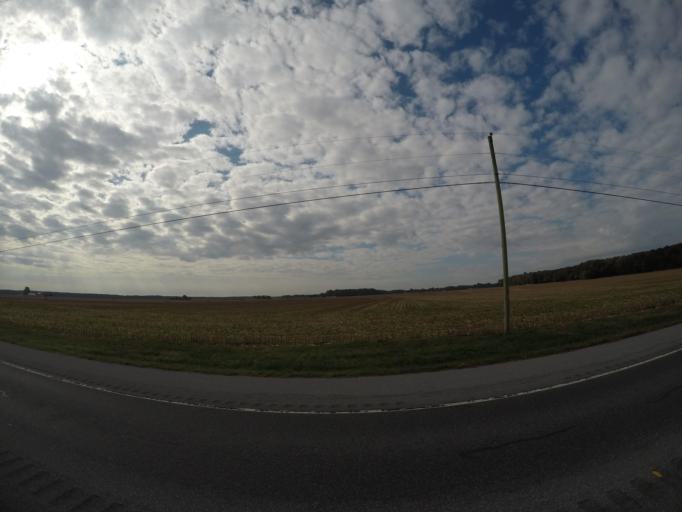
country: US
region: Delaware
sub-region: Sussex County
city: Bridgeville
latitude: 38.7144
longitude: -75.5732
